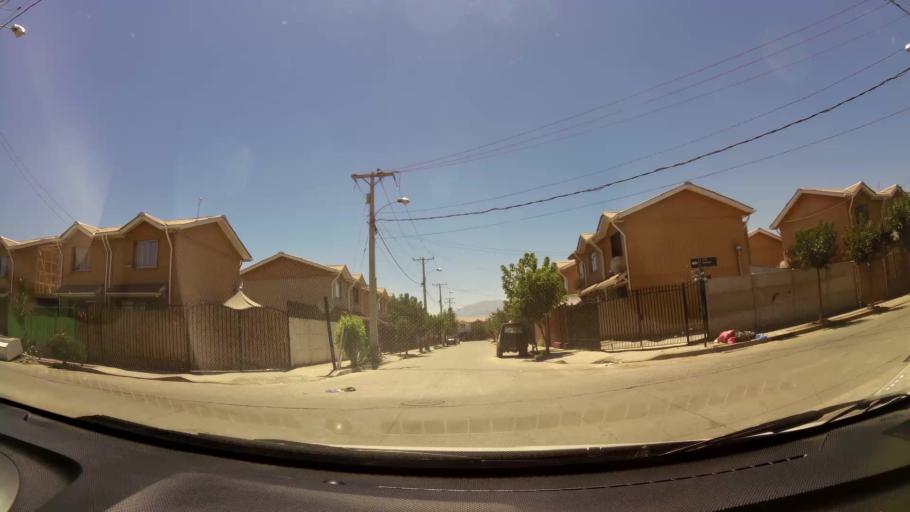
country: CL
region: O'Higgins
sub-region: Provincia de Cachapoal
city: Rancagua
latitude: -34.1530
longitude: -70.7101
